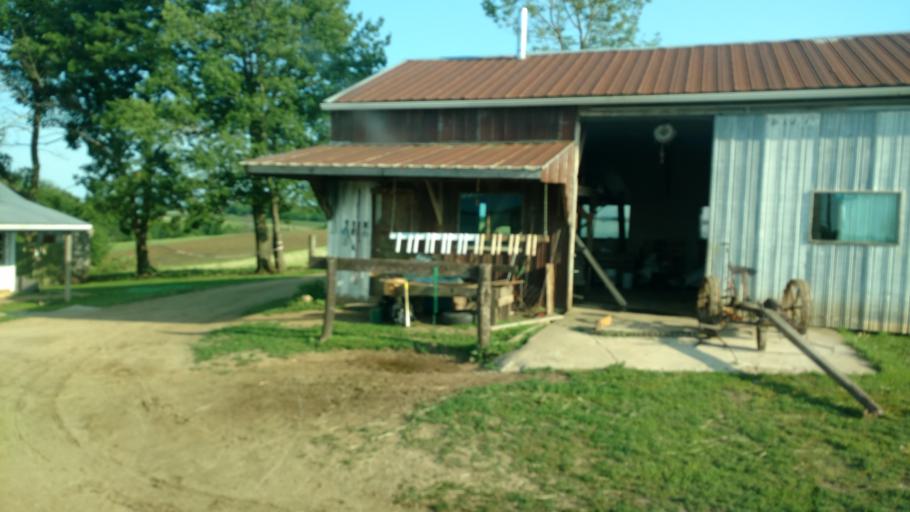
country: US
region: Wisconsin
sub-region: Vernon County
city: Hillsboro
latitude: 43.6265
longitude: -90.3294
